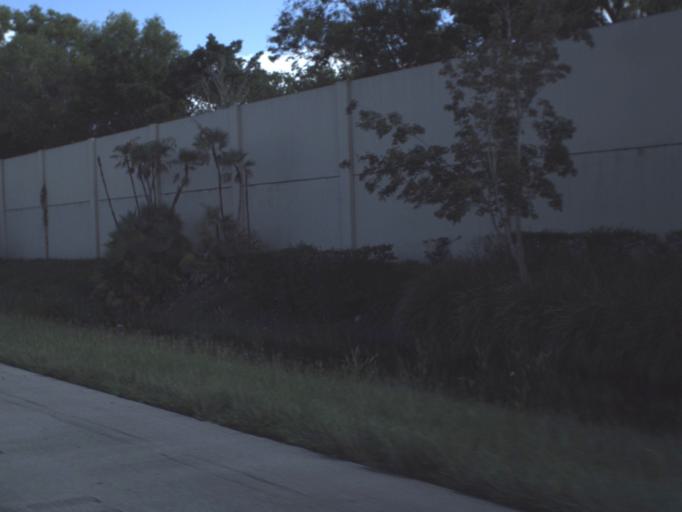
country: US
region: Florida
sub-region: Broward County
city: Coral Springs
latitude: 26.2495
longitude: -80.2970
